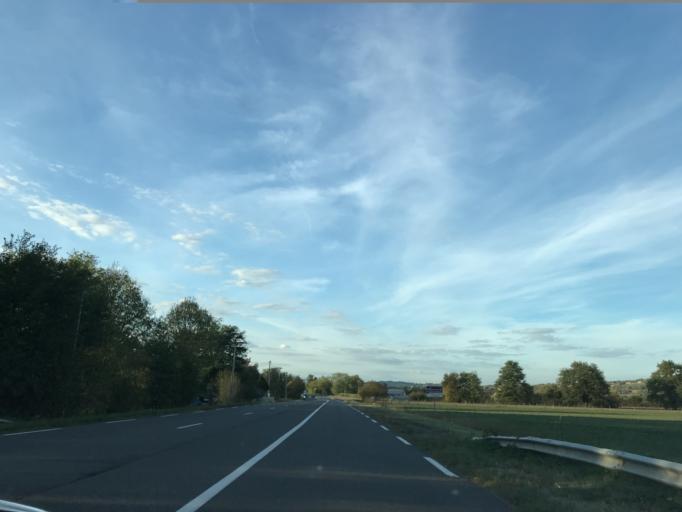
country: FR
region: Auvergne
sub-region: Departement de l'Allier
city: Saint-Yorre
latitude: 46.0386
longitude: 3.4749
